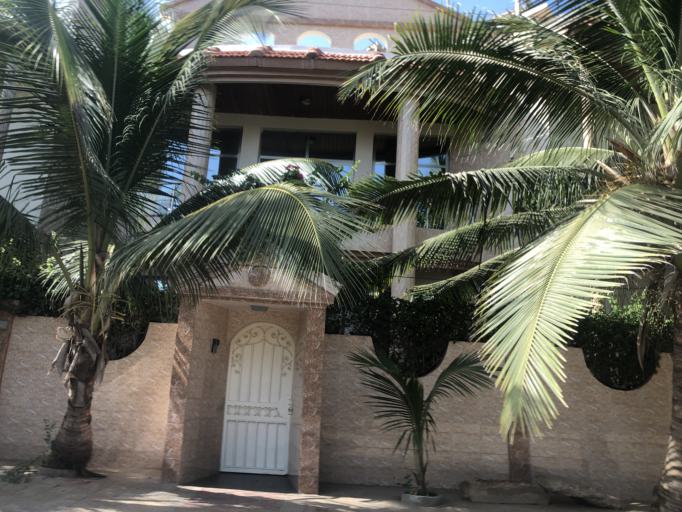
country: SN
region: Dakar
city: Mermoz Boabab
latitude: 14.7565
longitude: -17.4892
